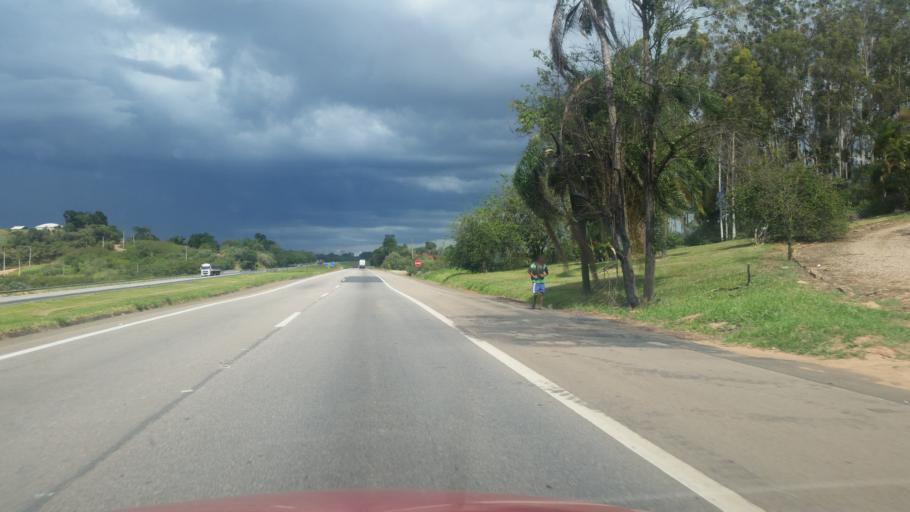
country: BR
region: Sao Paulo
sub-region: Boituva
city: Boituva
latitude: -23.2957
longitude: -47.7071
